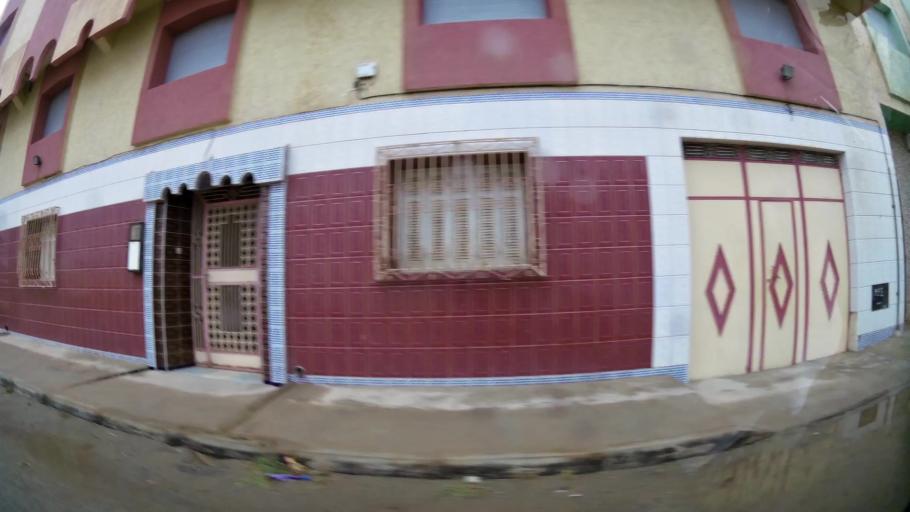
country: MA
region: Oriental
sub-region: Nador
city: Nador
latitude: 35.1549
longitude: -2.9607
